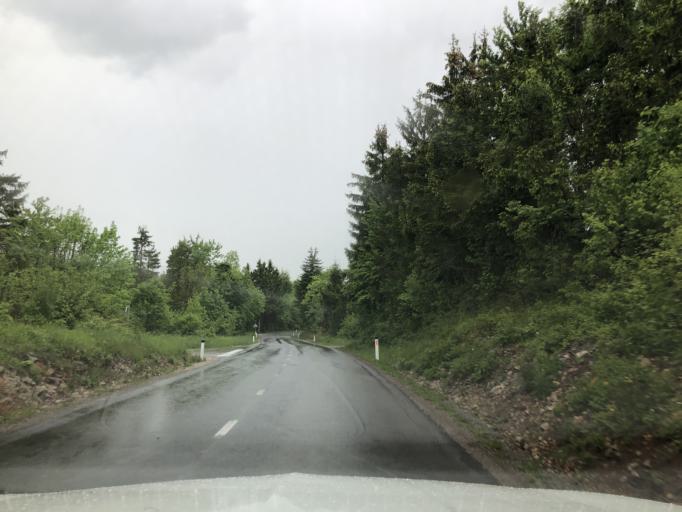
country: SI
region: Postojna
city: Postojna
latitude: 45.7952
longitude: 14.2427
